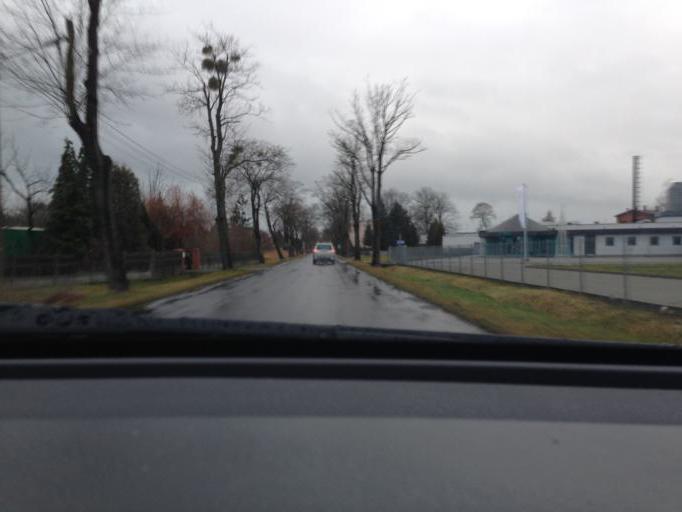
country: PL
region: Opole Voivodeship
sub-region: Powiat opolski
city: Wegry
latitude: 50.7293
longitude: 18.0396
